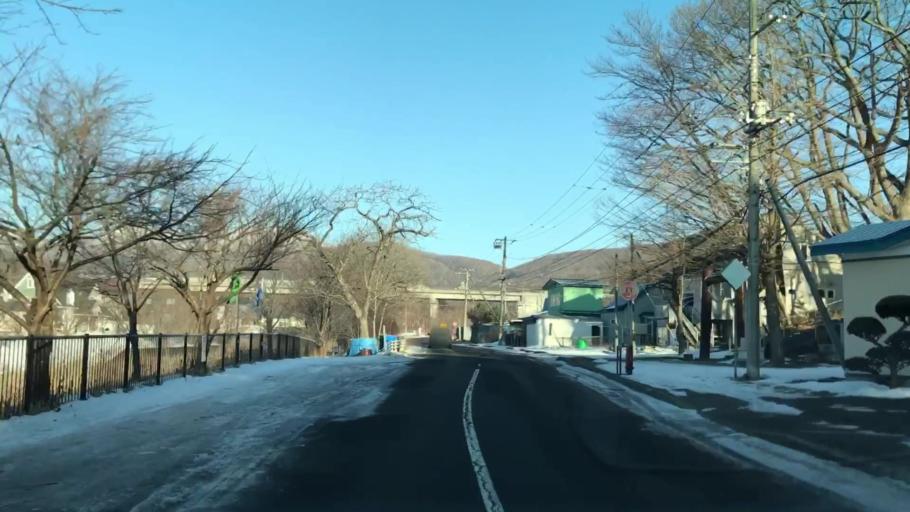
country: JP
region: Hokkaido
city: Muroran
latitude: 42.3879
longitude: 141.0692
